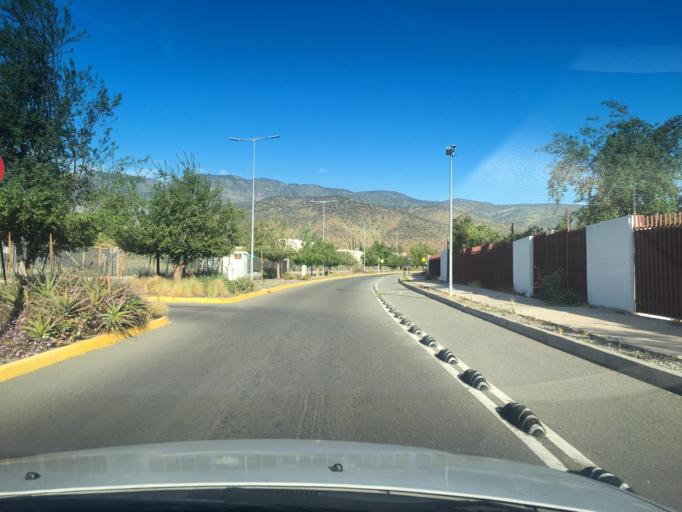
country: CL
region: Santiago Metropolitan
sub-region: Provincia de Chacabuco
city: Chicureo Abajo
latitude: -33.2577
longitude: -70.6219
